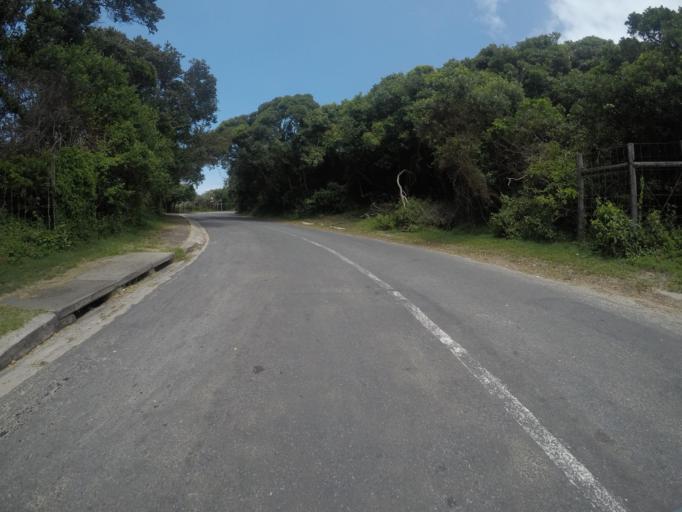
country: ZA
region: Eastern Cape
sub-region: Buffalo City Metropolitan Municipality
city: East London
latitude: -32.9938
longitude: 27.9485
